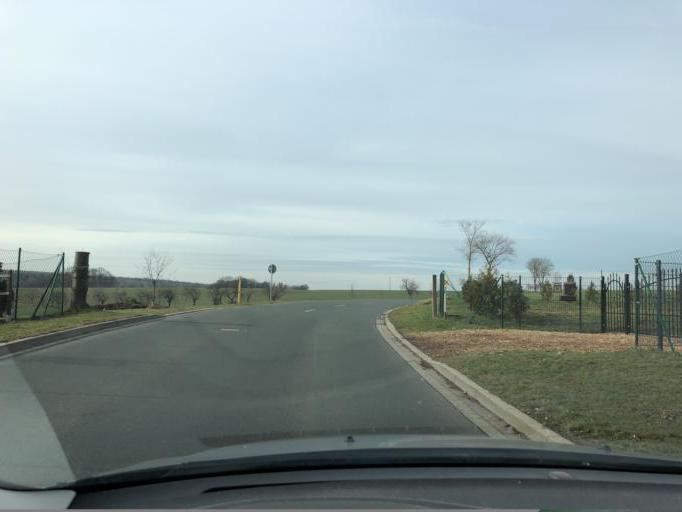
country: DE
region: Saxony-Anhalt
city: Bad Bibra
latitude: 51.1903
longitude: 11.5588
